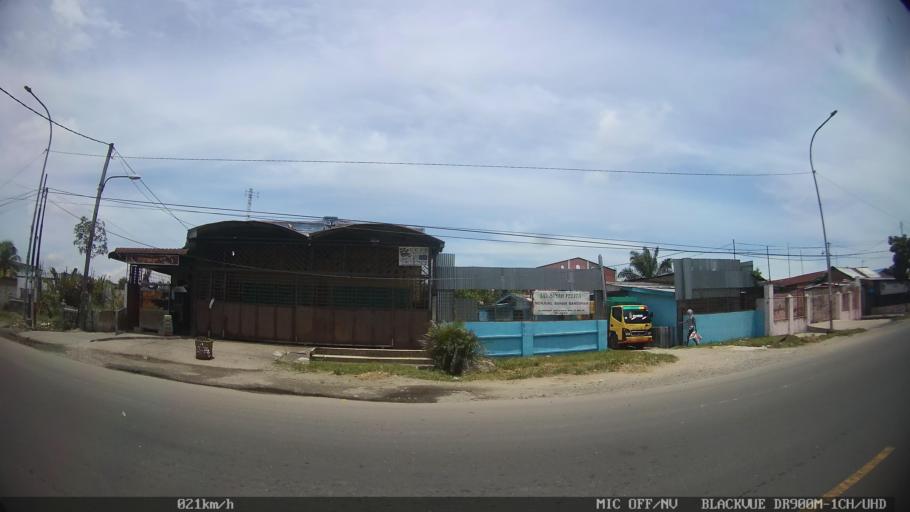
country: ID
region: North Sumatra
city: Belawan
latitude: 3.7577
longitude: 98.6784
